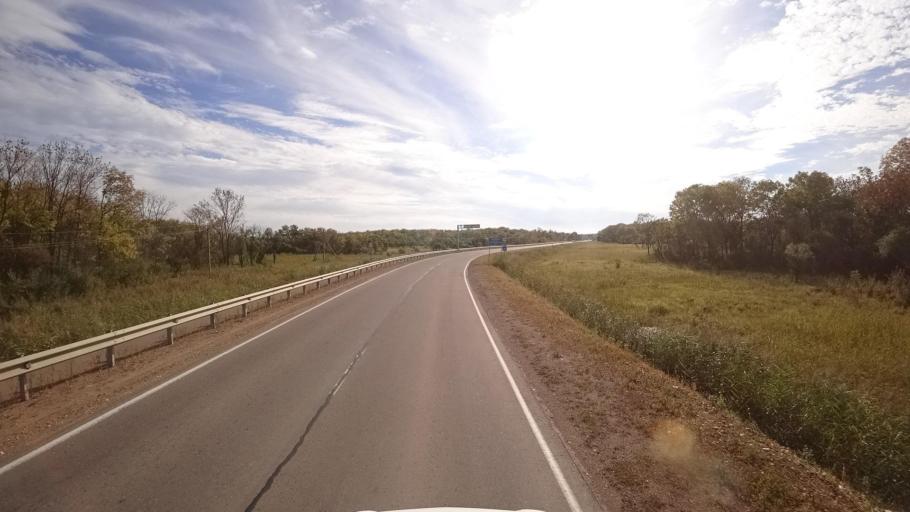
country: RU
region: Primorskiy
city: Dostoyevka
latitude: 44.2963
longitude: 133.4443
